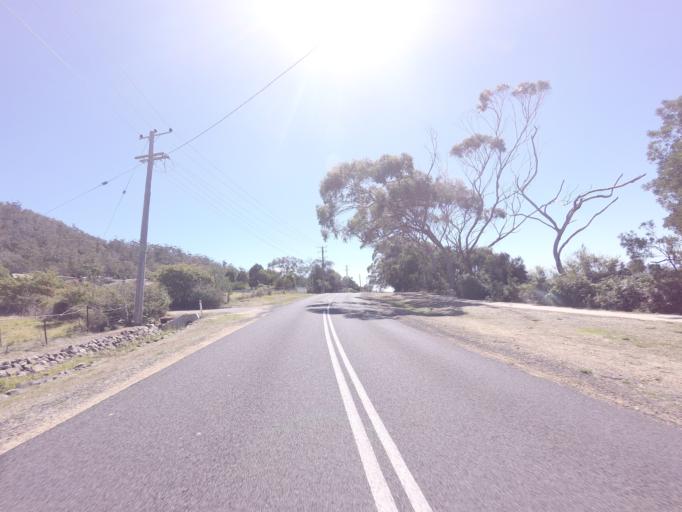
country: AU
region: Tasmania
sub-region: Break O'Day
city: St Helens
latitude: -41.8688
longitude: 148.2824
